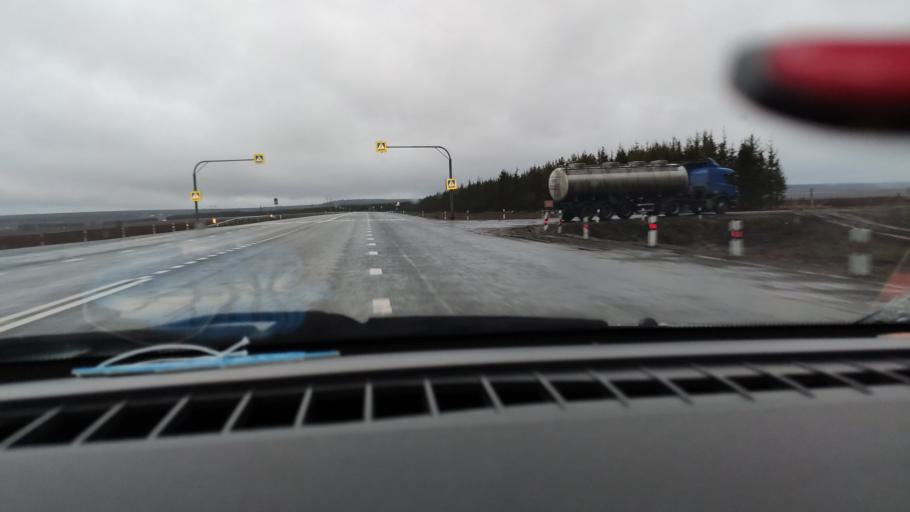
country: RU
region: Udmurtiya
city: Alnashi
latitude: 56.0845
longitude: 52.4186
